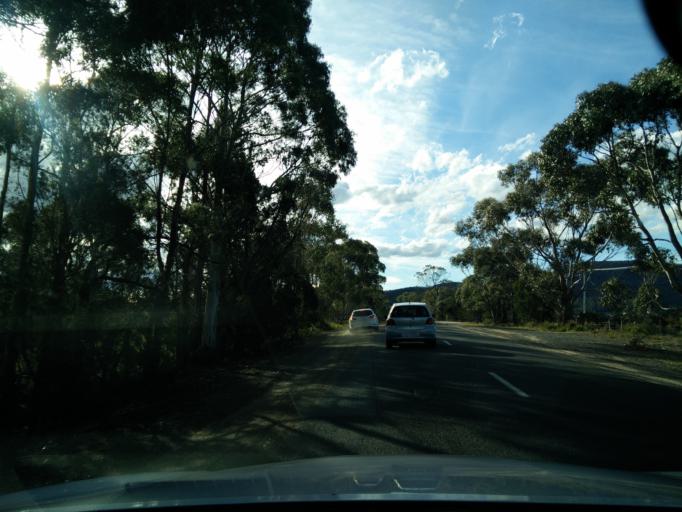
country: AU
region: Tasmania
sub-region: Break O'Day
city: St Helens
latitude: -41.9415
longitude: 148.2302
